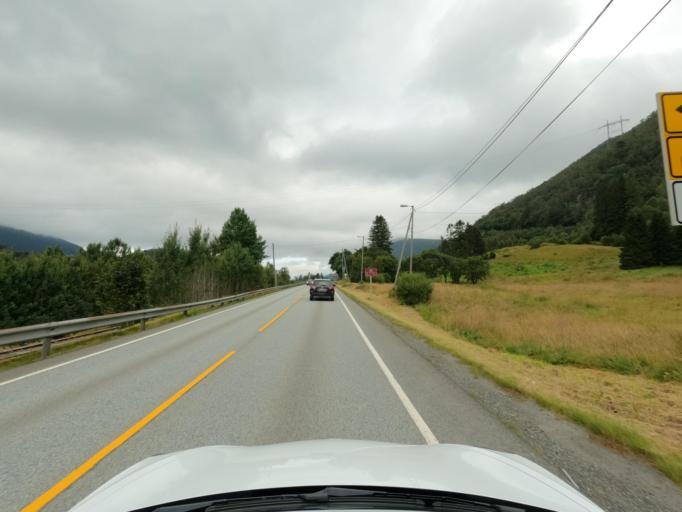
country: NO
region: Hordaland
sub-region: Bergen
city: Espeland
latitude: 60.3919
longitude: 5.4724
